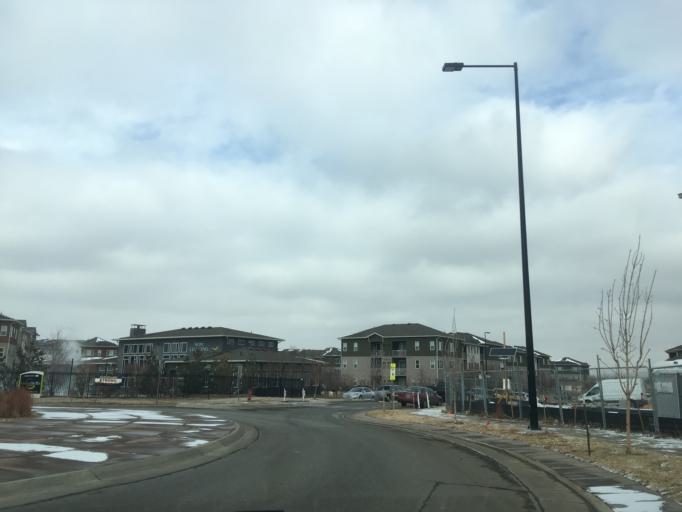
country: US
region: Colorado
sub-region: Boulder County
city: Lafayette
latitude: 39.9733
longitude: -105.0841
